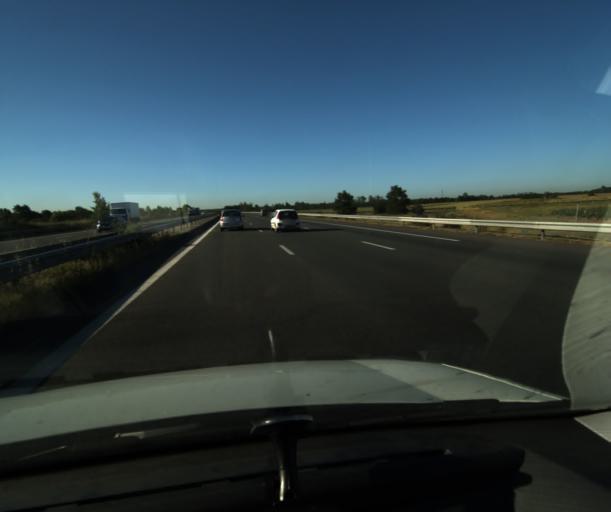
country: FR
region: Midi-Pyrenees
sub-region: Departement du Tarn-et-Garonne
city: Campsas
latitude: 43.8782
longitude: 1.3168
